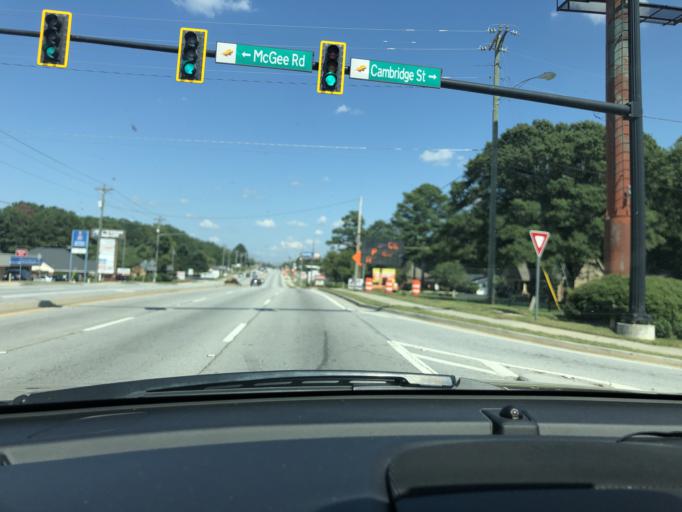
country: US
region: Georgia
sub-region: Gwinnett County
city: Snellville
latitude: 33.8537
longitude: -84.0333
